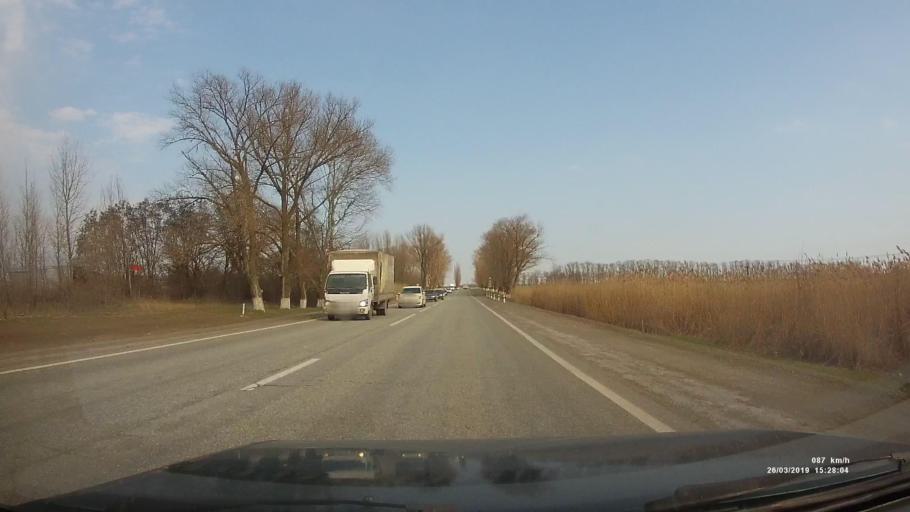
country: RU
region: Rostov
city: Primorka
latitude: 47.3219
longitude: 39.0765
